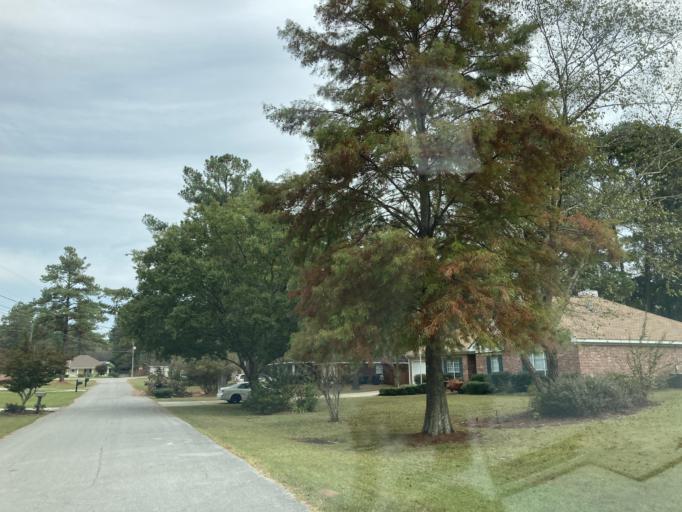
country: US
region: Mississippi
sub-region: Lamar County
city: West Hattiesburg
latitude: 31.2828
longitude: -89.3637
